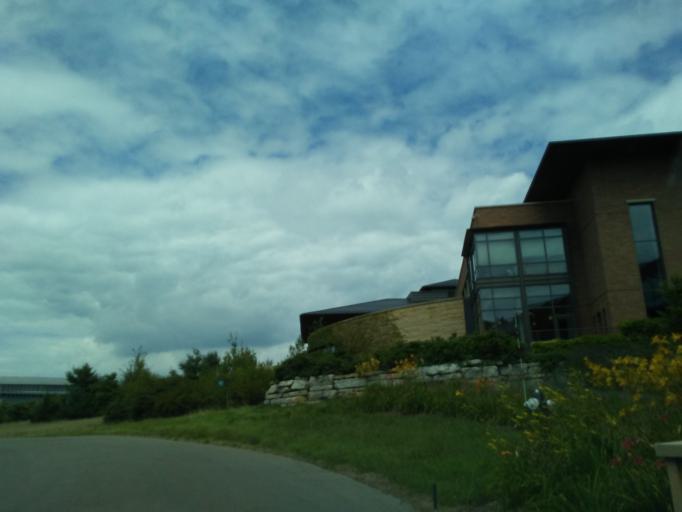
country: US
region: Wisconsin
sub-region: Dane County
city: Verona
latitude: 42.9941
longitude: -89.5672
